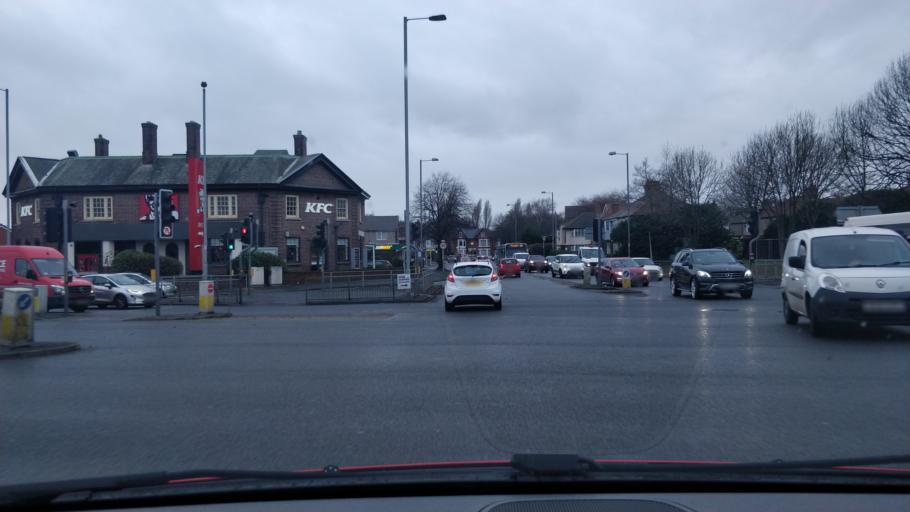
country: GB
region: England
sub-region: Sefton
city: Litherland
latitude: 53.4698
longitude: -2.9979
